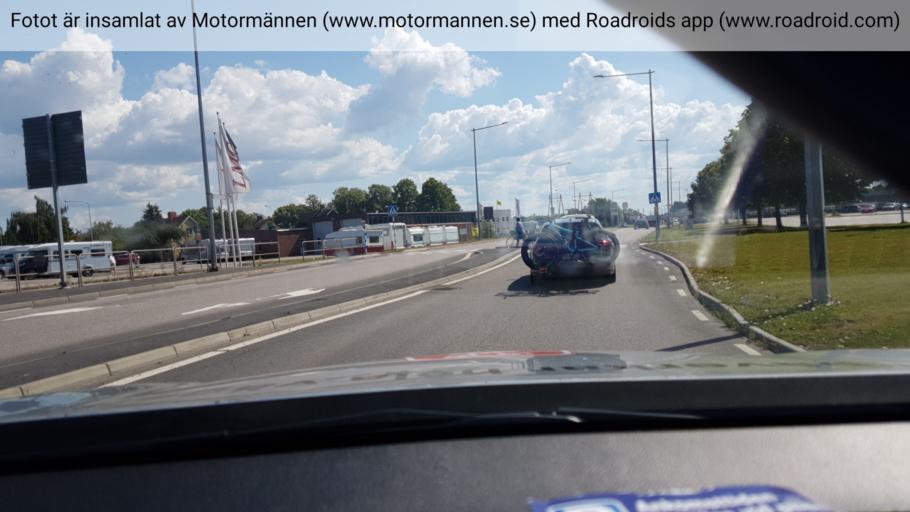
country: SE
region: Vaestra Goetaland
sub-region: Lidkopings Kommun
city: Lidkoping
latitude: 58.4998
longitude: 13.1803
